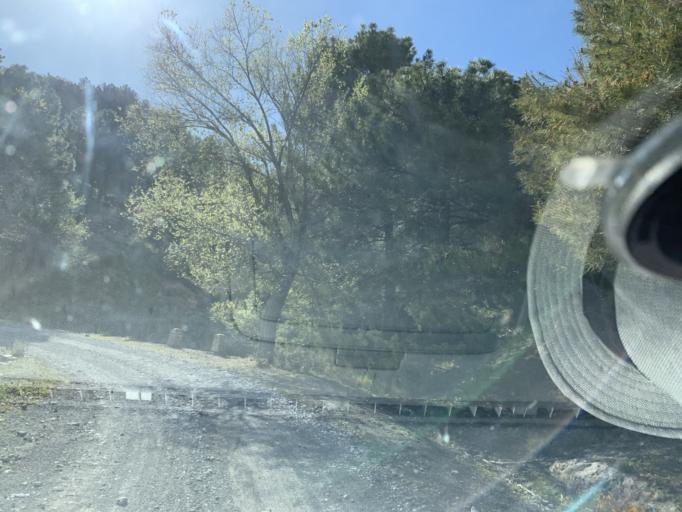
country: ES
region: Andalusia
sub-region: Provincia de Granada
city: Beas de Granada
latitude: 37.2373
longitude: -3.4293
